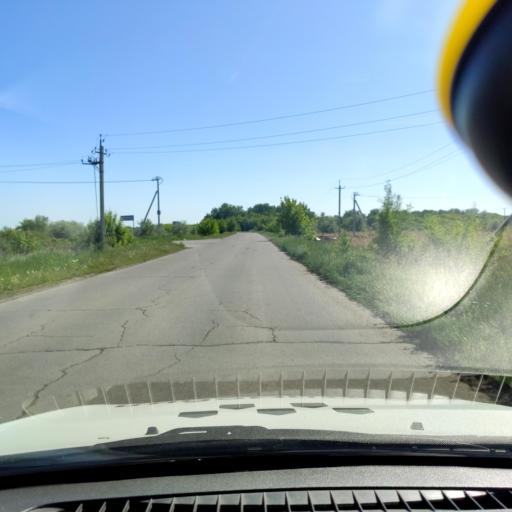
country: RU
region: Samara
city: Tol'yatti
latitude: 53.6454
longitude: 49.3179
